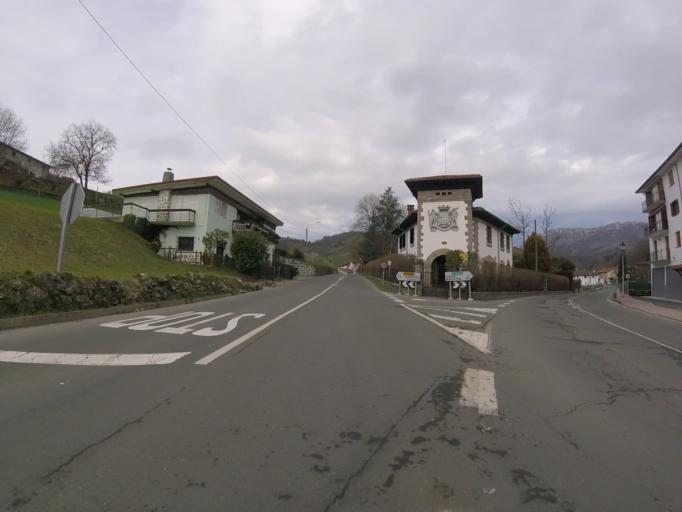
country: ES
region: Basque Country
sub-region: Provincia de Guipuzcoa
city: Albiztur
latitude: 43.1379
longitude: -2.1609
